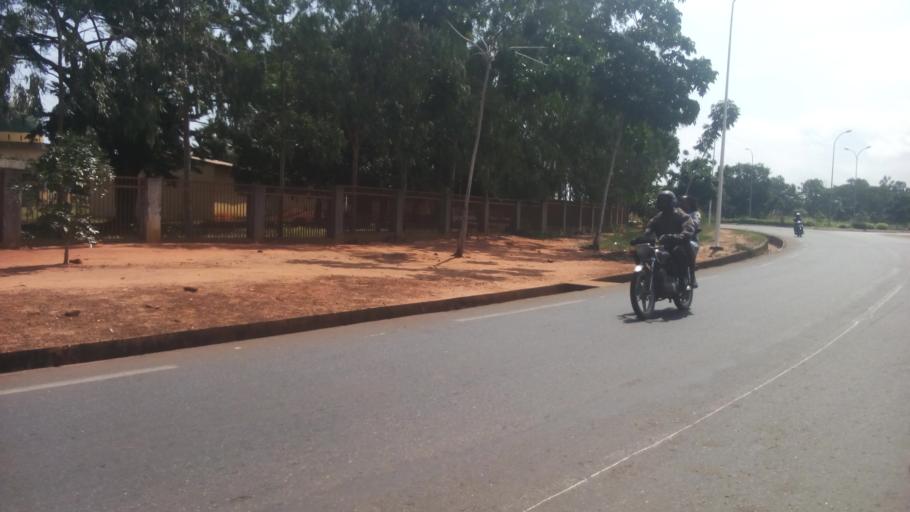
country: TG
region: Maritime
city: Lome
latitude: 6.1927
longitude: 1.2280
